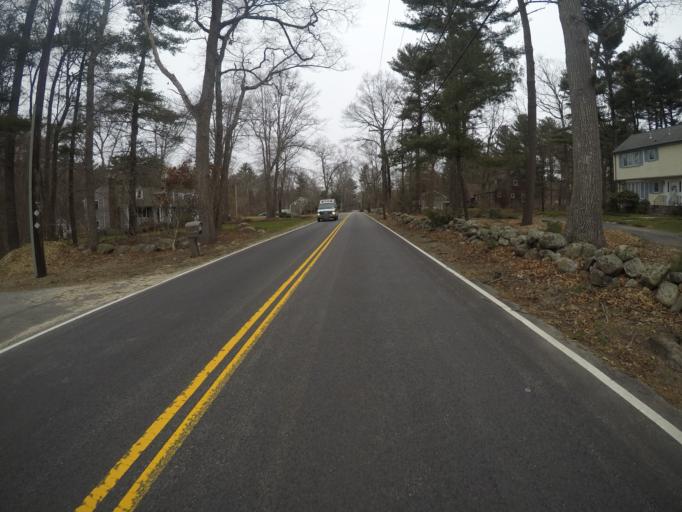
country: US
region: Massachusetts
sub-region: Bristol County
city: Easton
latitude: 42.0482
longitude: -71.1419
